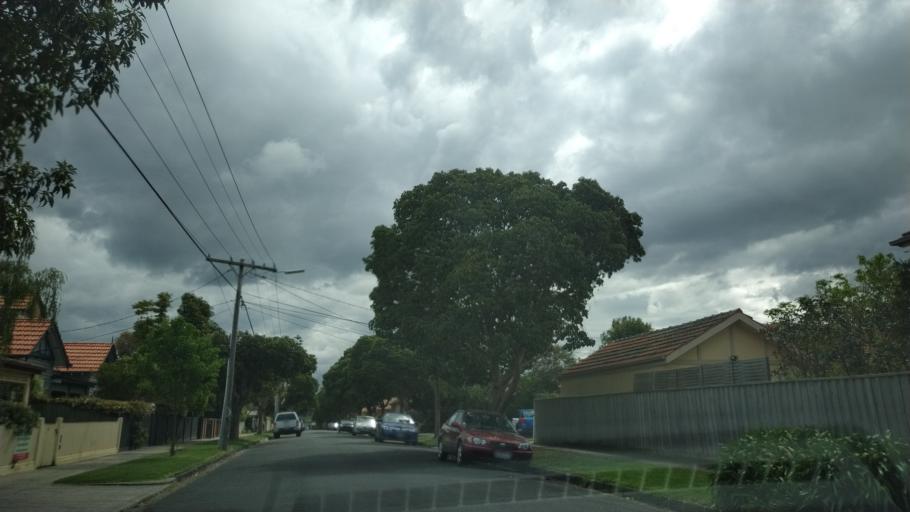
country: AU
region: Victoria
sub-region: Glen Eira
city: Carnegie
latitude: -37.8931
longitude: 145.0630
